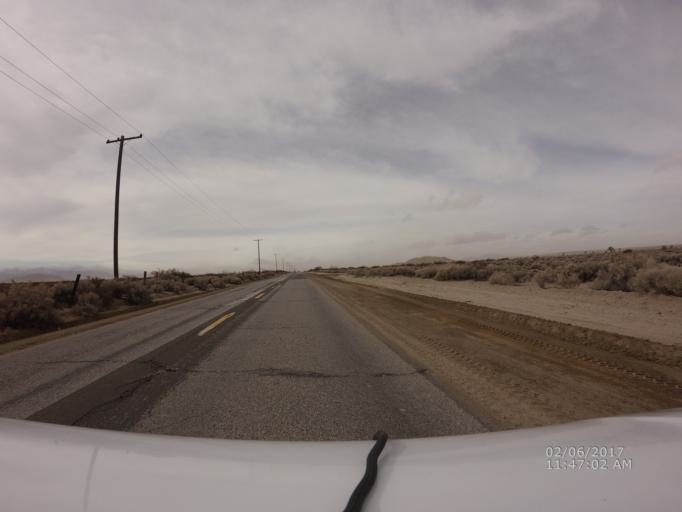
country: US
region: California
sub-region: Los Angeles County
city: Lake Los Angeles
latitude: 34.6021
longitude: -117.6725
